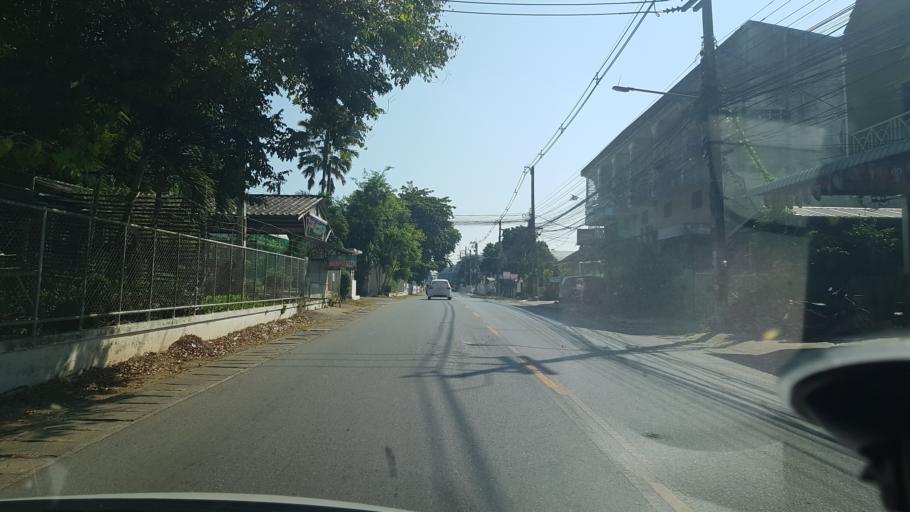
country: TH
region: Chiang Rai
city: Chiang Rai
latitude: 19.9048
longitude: 99.8109
